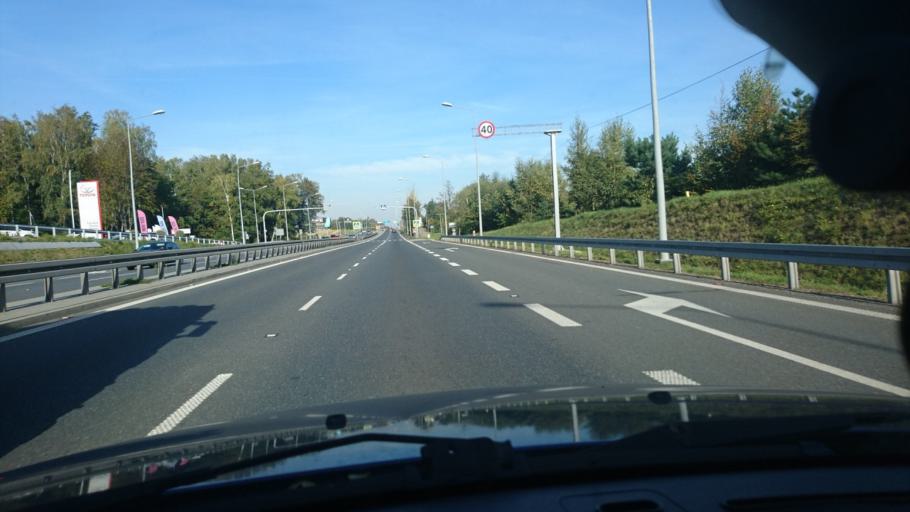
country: PL
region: Silesian Voivodeship
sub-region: Powiat bielski
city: Mazancowice
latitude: 49.8676
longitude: 19.0097
